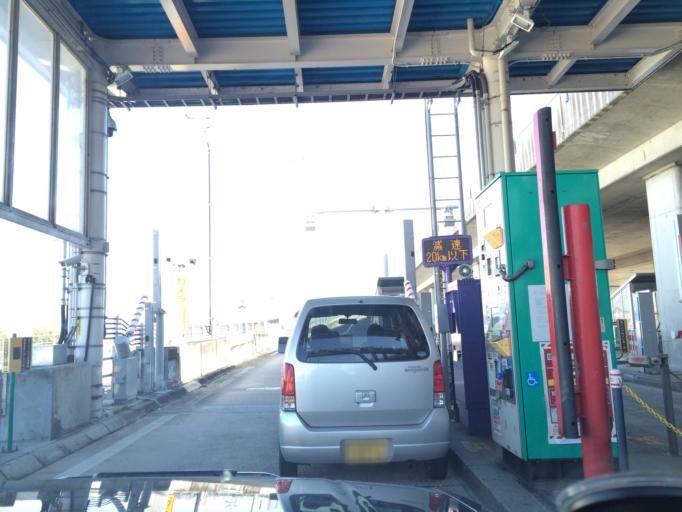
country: JP
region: Kyoto
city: Tanabe
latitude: 34.8392
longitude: 135.7546
